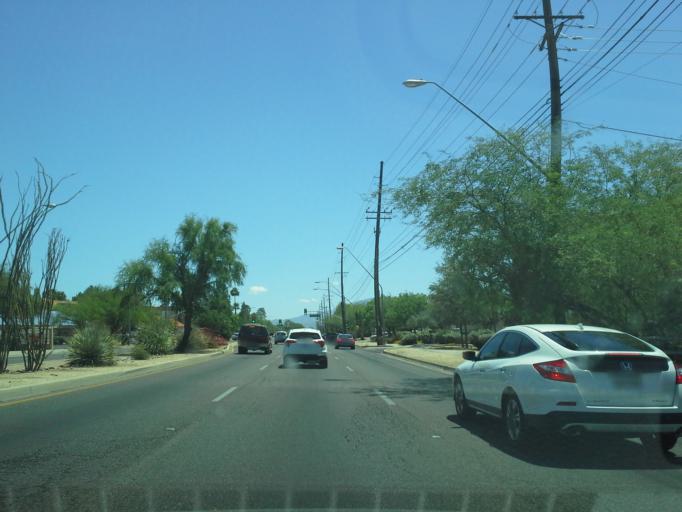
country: US
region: Arizona
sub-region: Pima County
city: Tucson
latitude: 32.2506
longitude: -110.8856
